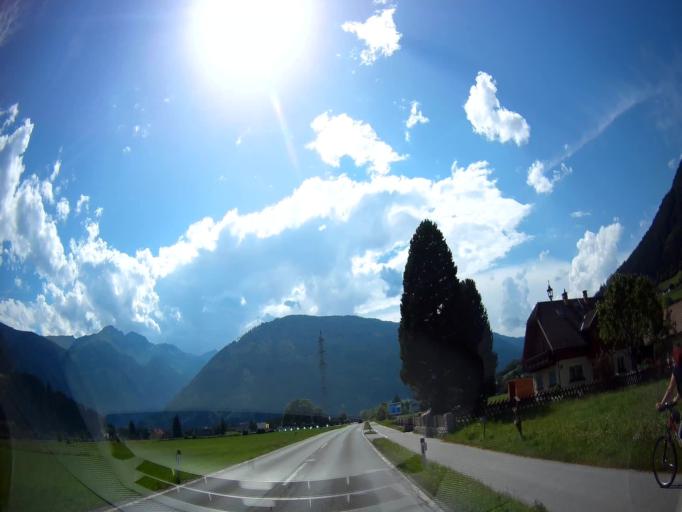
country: AT
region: Salzburg
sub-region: Politischer Bezirk Tamsweg
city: Sankt Michael im Lungau
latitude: 47.0969
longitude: 13.6213
